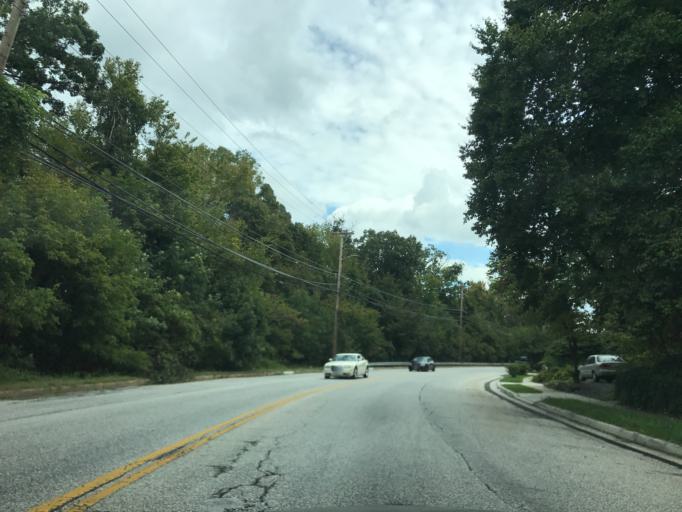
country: US
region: Maryland
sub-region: Baltimore County
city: Woodlawn
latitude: 39.3256
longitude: -76.7196
